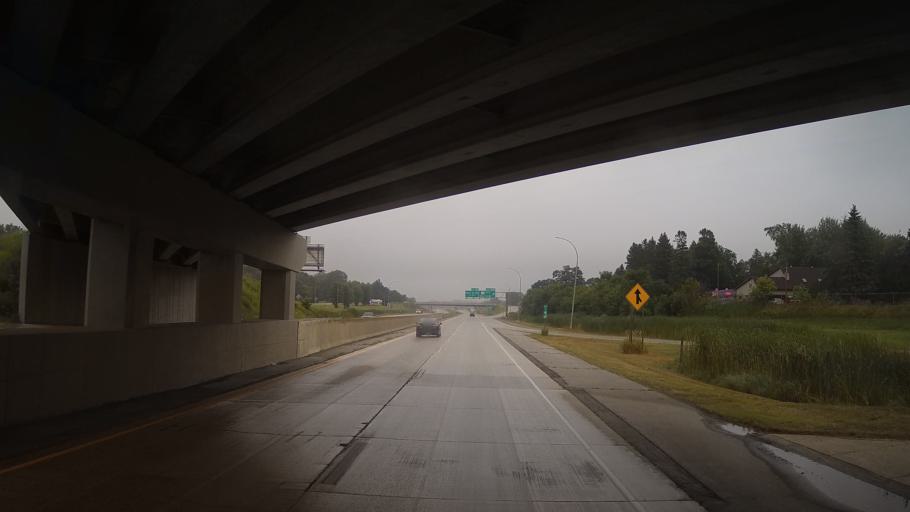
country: US
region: Minnesota
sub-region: Mower County
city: Austin
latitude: 43.6742
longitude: -92.9462
